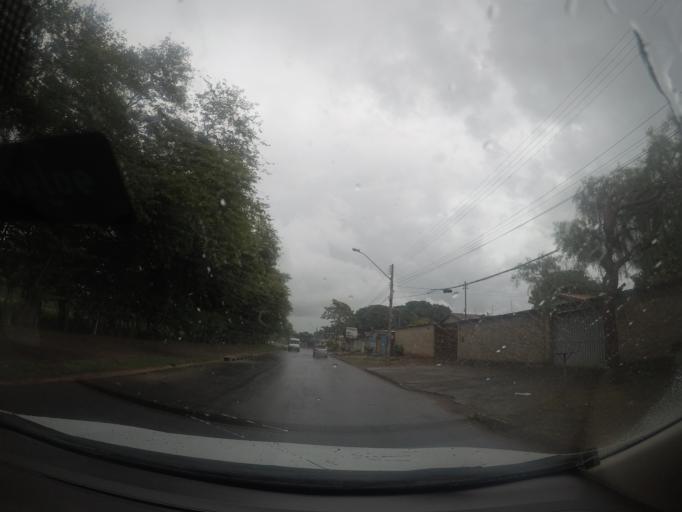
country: BR
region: Goias
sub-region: Trindade
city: Trindade
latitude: -16.6470
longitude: -49.3898
